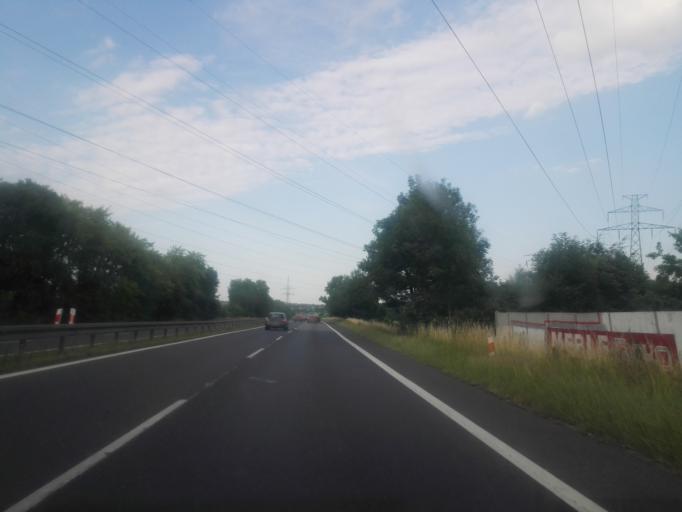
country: PL
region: Silesian Voivodeship
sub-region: Powiat bedzinski
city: Psary
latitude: 50.3528
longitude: 19.1135
